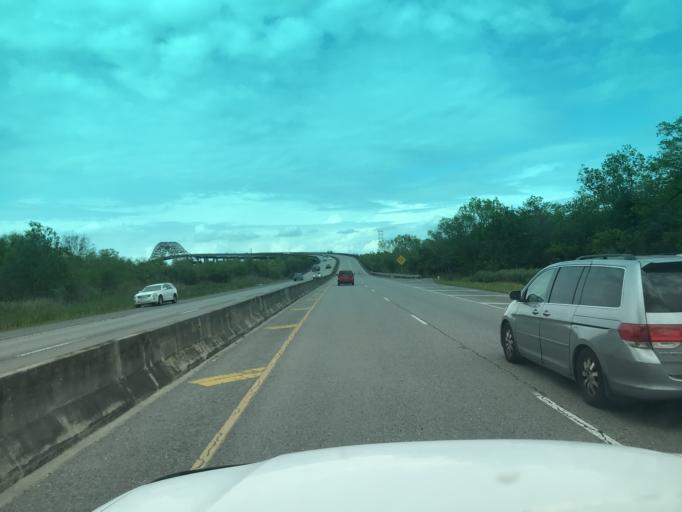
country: US
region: Louisiana
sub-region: Saint Bernard Parish
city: Chalmette
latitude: 29.9950
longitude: -89.9405
